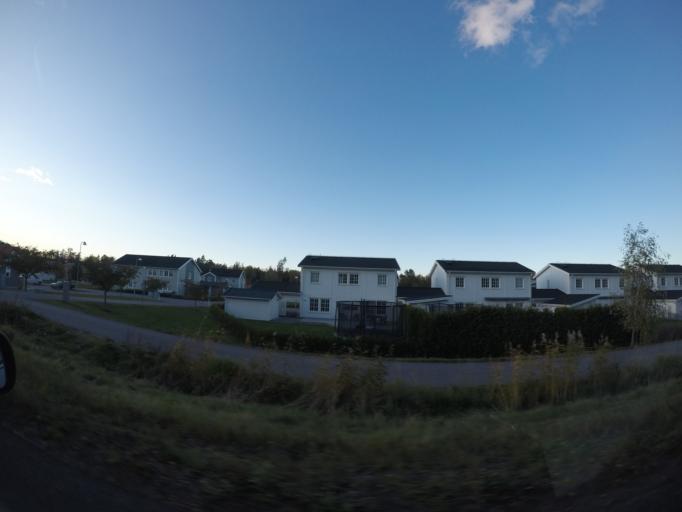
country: SE
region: Vaestmanland
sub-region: Vasteras
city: Vasteras
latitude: 59.5581
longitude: 16.5001
